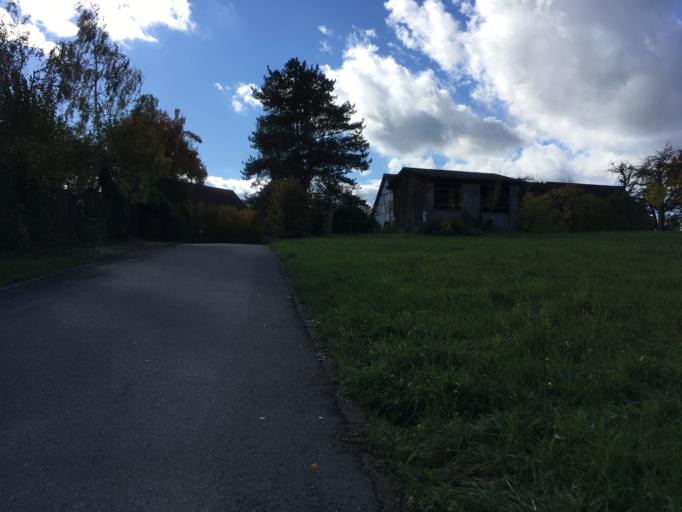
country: DE
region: Baden-Wuerttemberg
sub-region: Regierungsbezirk Stuttgart
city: Pfedelbach
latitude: 49.1801
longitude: 9.4815
